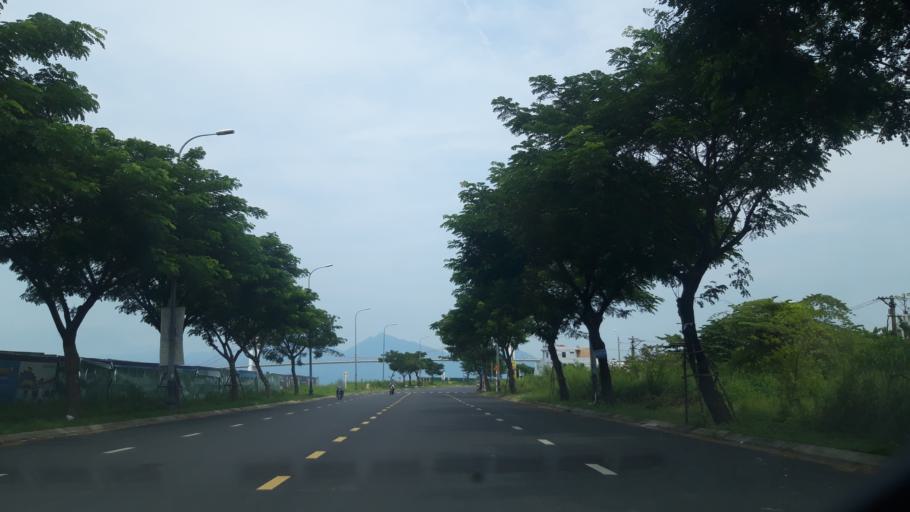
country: VN
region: Da Nang
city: Da Nang
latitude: 16.0891
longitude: 108.2282
